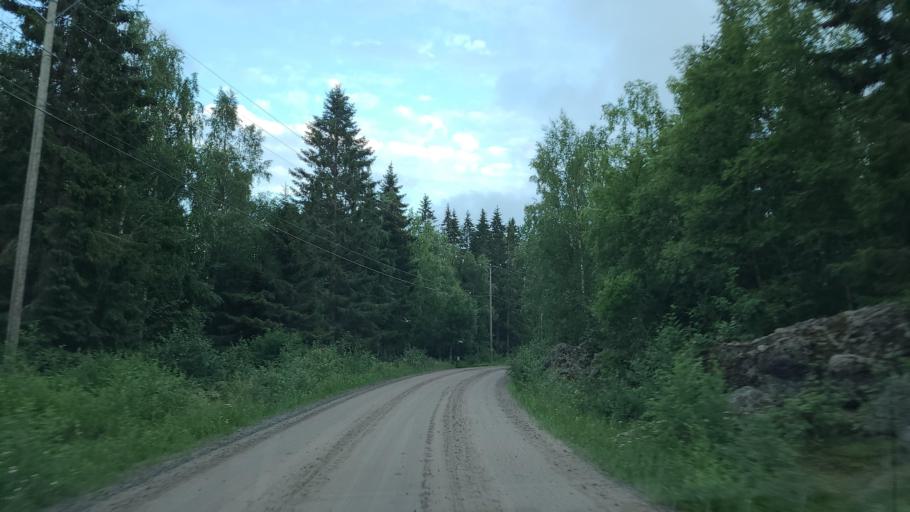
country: FI
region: Ostrobothnia
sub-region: Vaasa
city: Replot
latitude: 63.3039
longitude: 21.1538
